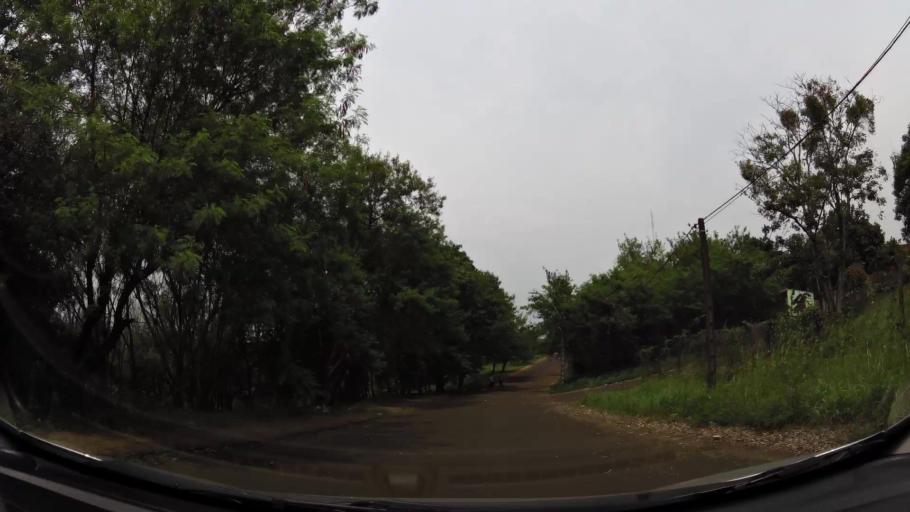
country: PY
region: Alto Parana
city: Presidente Franco
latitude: -25.5498
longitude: -54.6131
